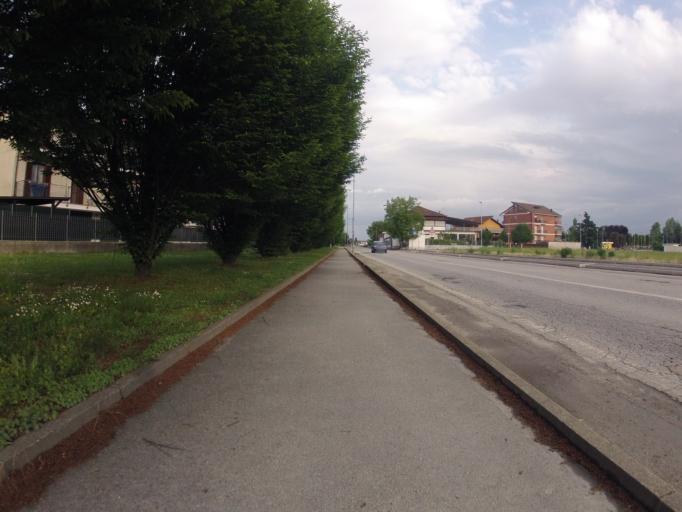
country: IT
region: Piedmont
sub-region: Provincia di Cuneo
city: Moretta
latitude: 44.7600
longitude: 7.5339
